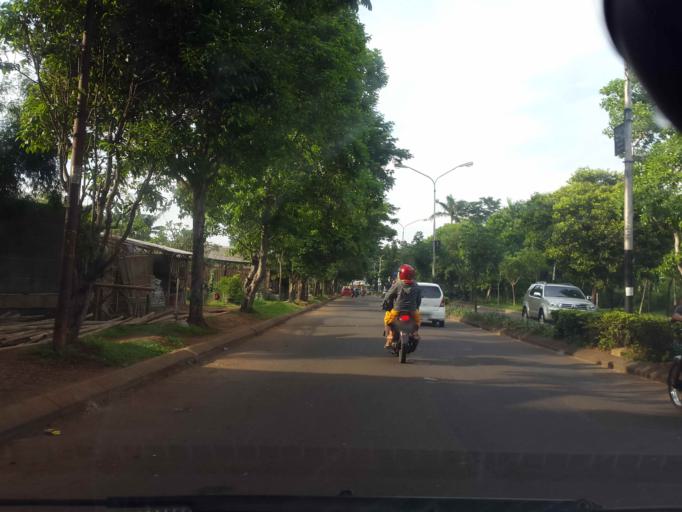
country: ID
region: West Java
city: Ciputat
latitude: -6.2649
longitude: 106.6880
